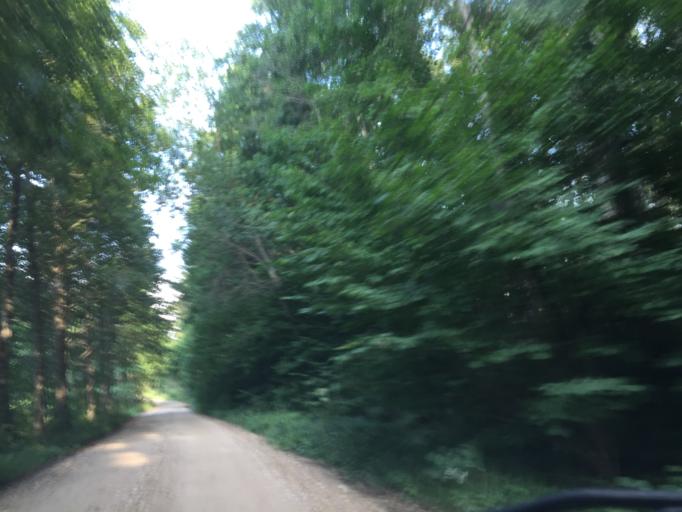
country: LT
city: Zagare
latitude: 56.4490
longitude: 23.1408
